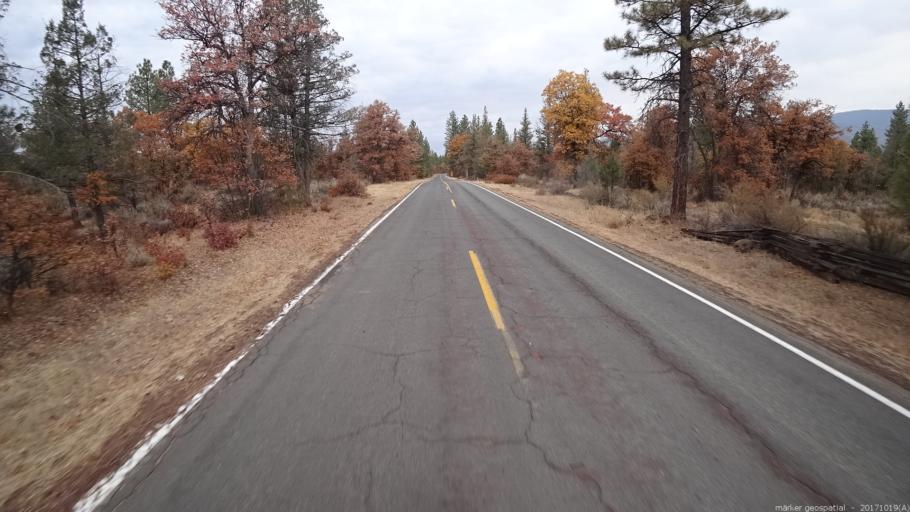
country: US
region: California
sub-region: Shasta County
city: Burney
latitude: 41.1111
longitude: -121.3303
